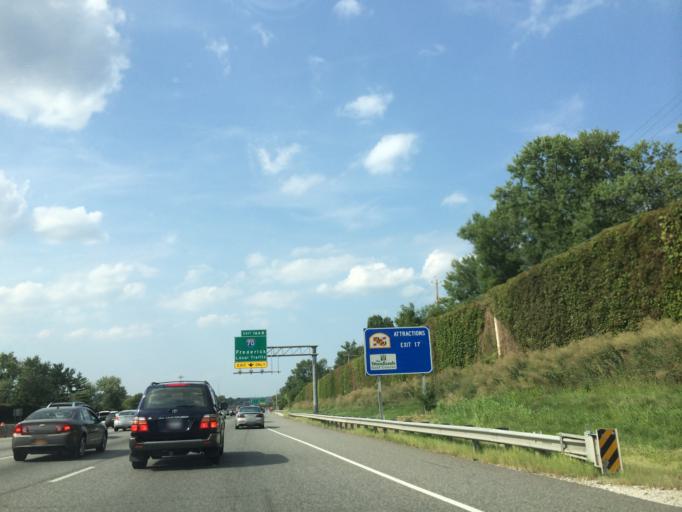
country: US
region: Maryland
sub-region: Baltimore County
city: Catonsville
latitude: 39.2920
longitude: -76.7421
